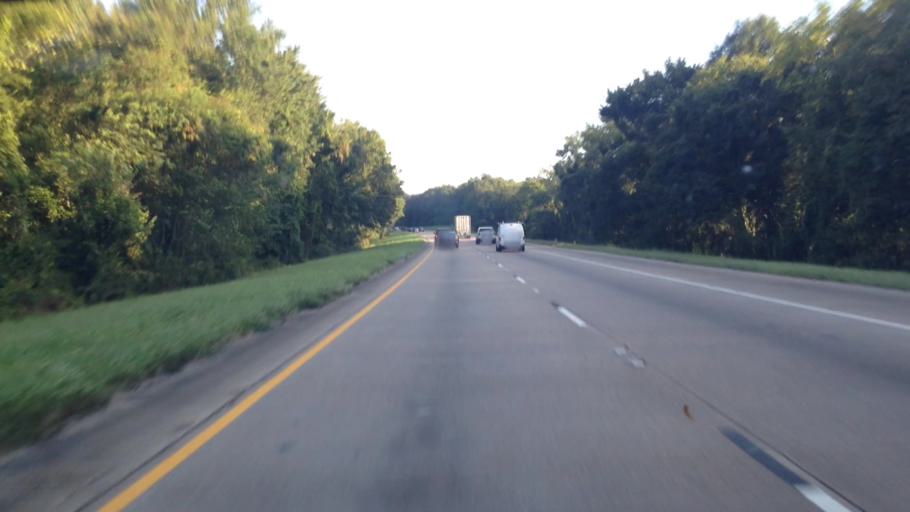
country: US
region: Louisiana
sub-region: Ascension Parish
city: Prairieville
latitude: 30.3040
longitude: -90.9929
